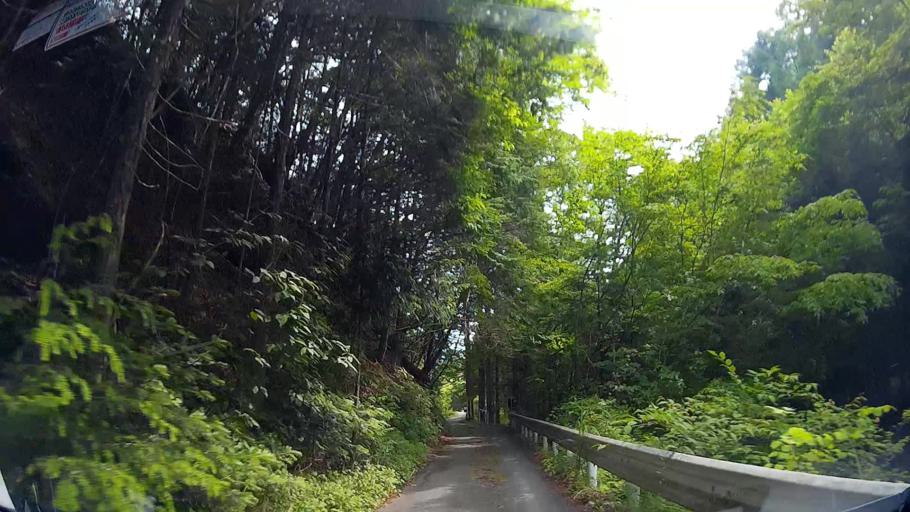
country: JP
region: Nagano
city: Iida
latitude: 35.4655
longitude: 138.0007
